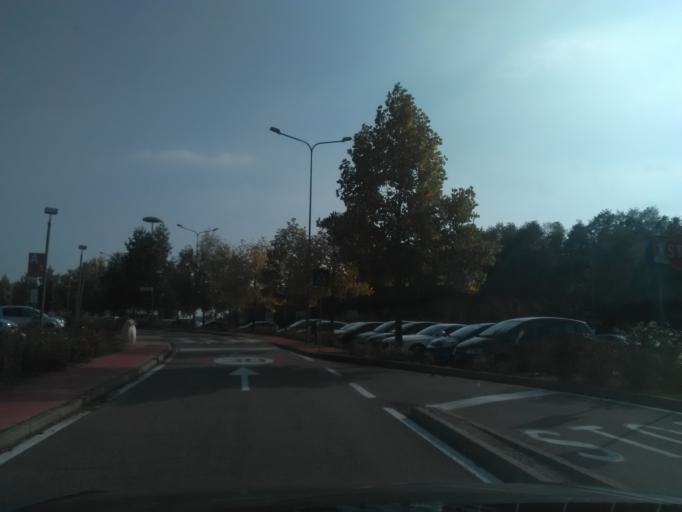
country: IT
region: Piedmont
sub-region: Provincia di Biella
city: Gaglianico
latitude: 45.5473
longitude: 8.0746
